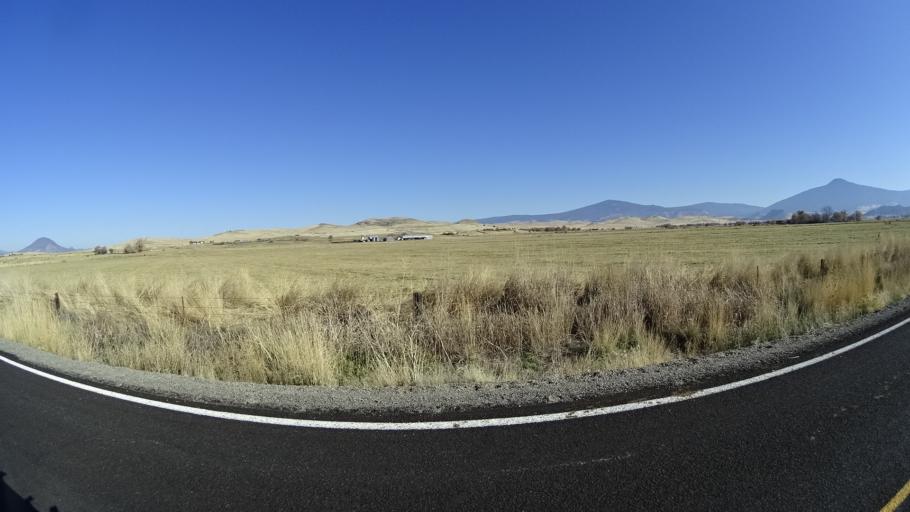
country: US
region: California
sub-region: Siskiyou County
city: Montague
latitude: 41.7161
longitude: -122.4456
